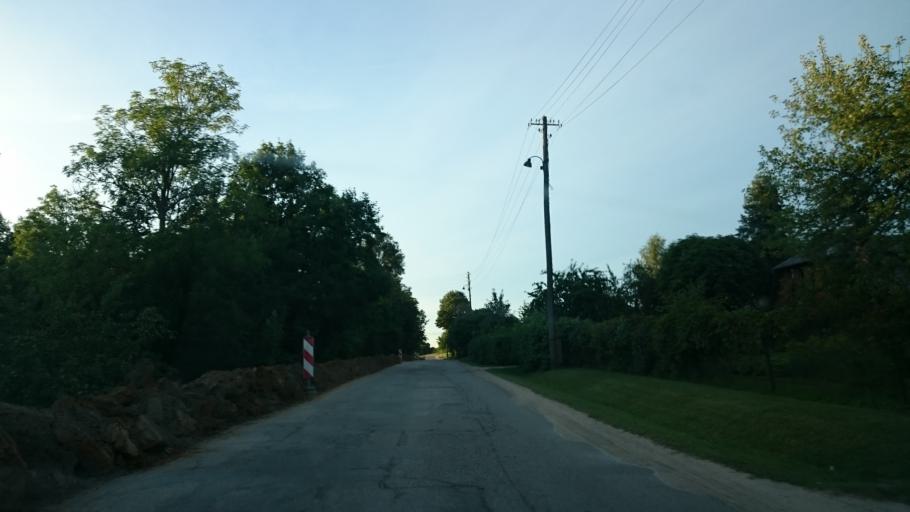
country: LV
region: Saldus Rajons
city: Saldus
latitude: 56.6728
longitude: 22.4950
